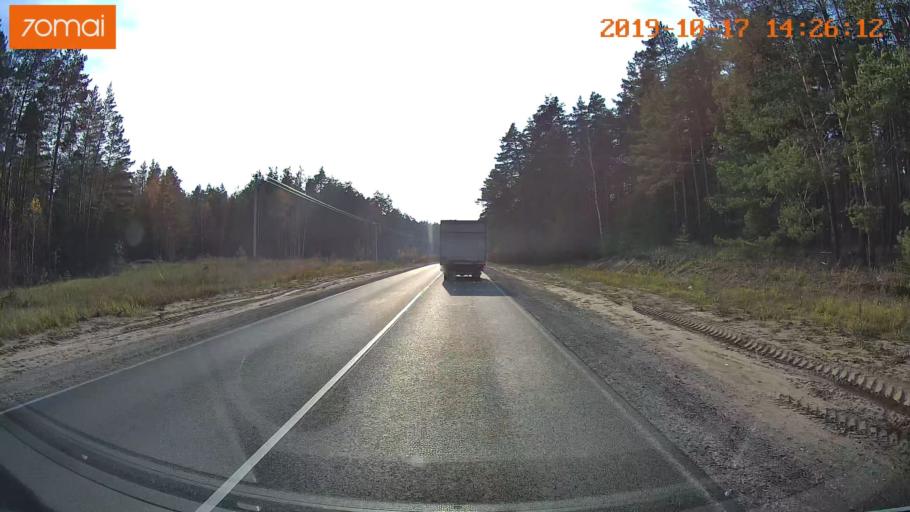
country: RU
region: Moskovskaya
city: Radovitskiy
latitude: 54.9939
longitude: 39.9700
